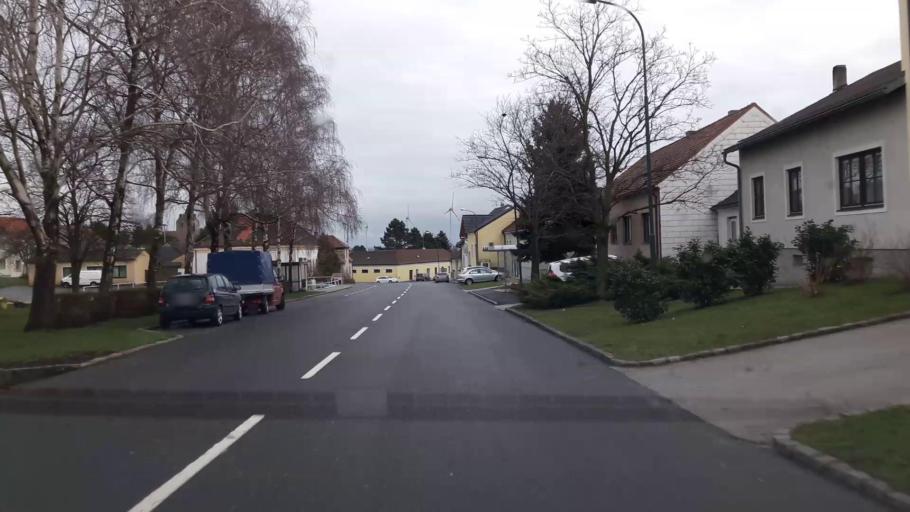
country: AT
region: Lower Austria
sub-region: Politischer Bezirk Bruck an der Leitha
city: Scharndorf
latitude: 48.0945
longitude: 16.7976
